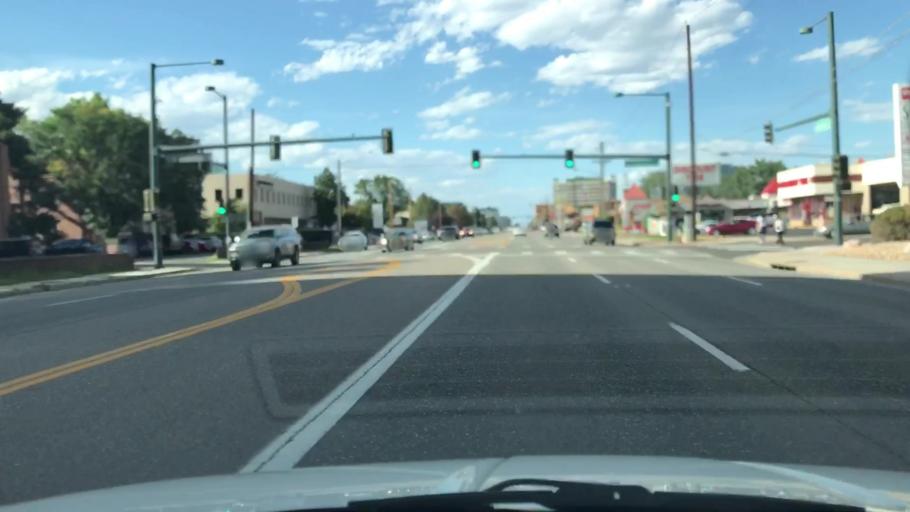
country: US
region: Colorado
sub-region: Arapahoe County
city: Glendale
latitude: 39.6715
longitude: -104.9407
